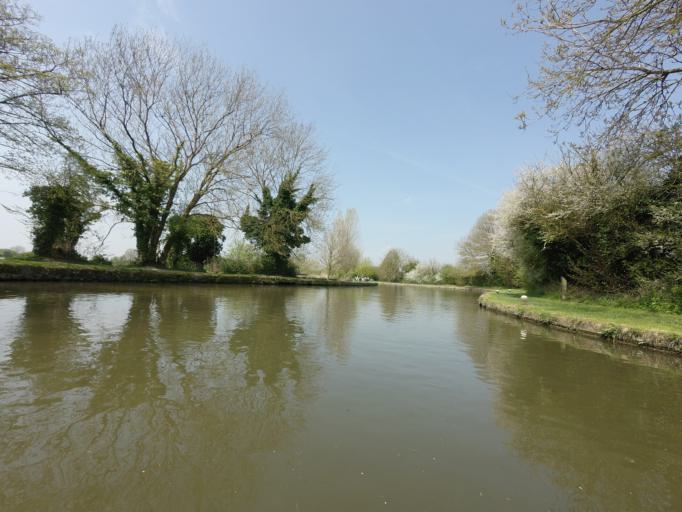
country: GB
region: England
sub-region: Hertfordshire
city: Tring
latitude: 51.8161
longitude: -0.6601
